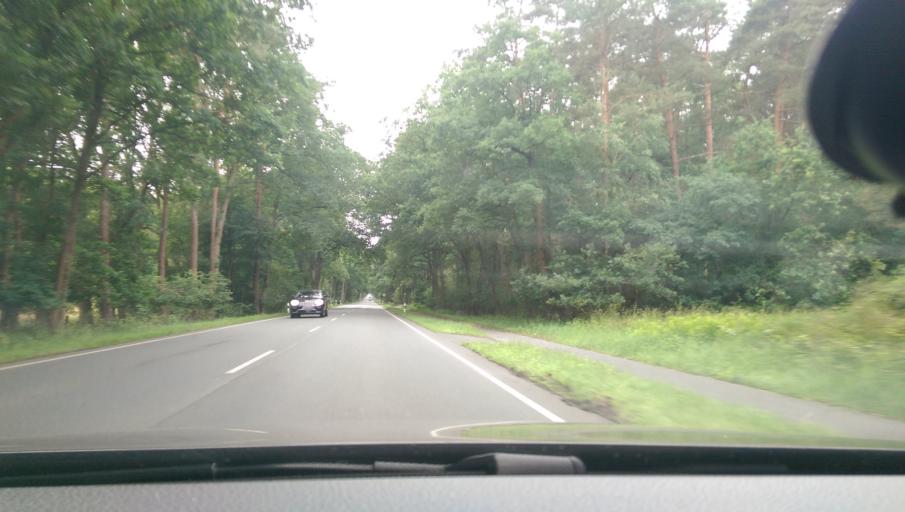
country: DE
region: Lower Saxony
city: Ahausen
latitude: 53.0556
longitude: 9.3380
